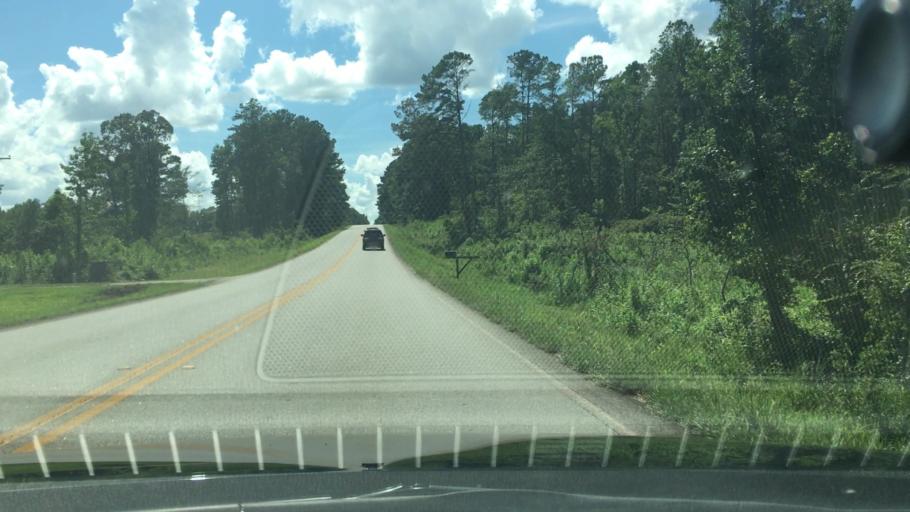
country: US
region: Georgia
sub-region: Jasper County
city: Monticello
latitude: 33.3050
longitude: -83.6144
